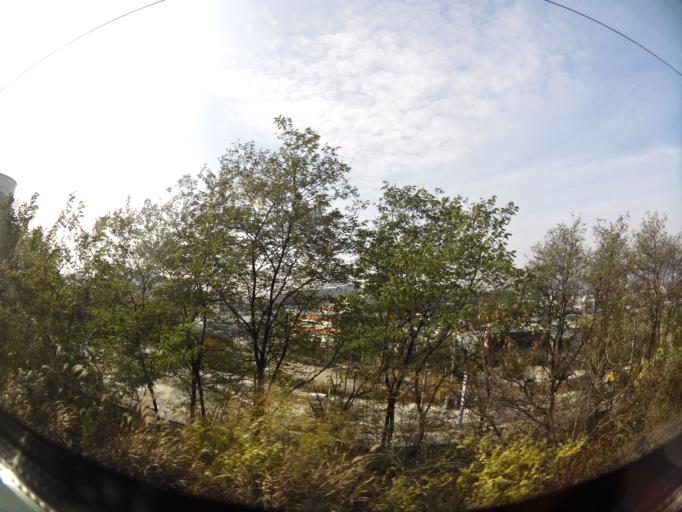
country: KR
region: Daejeon
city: Sintansin
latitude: 36.5251
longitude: 127.3736
